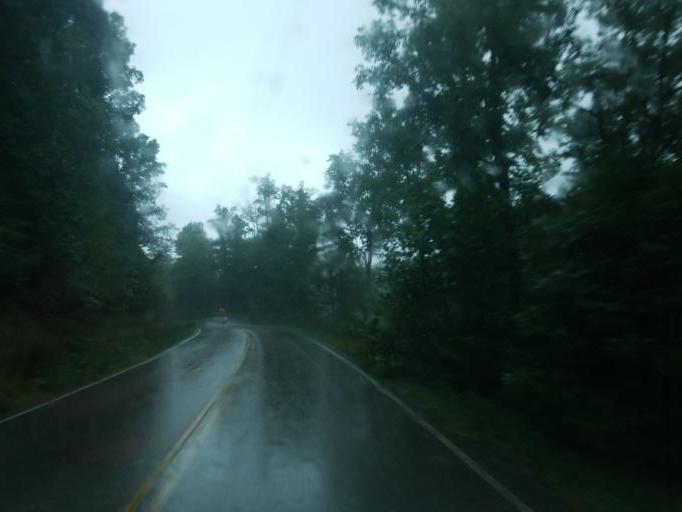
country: US
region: Kentucky
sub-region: Carter County
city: Olive Hill
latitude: 38.3402
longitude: -83.2006
